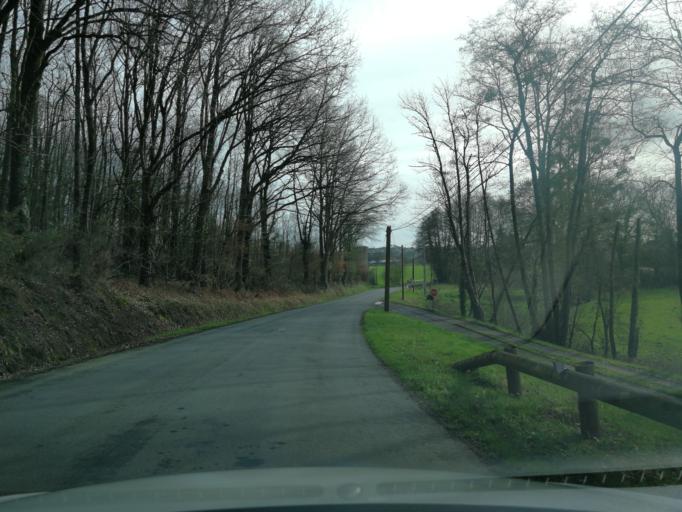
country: FR
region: Brittany
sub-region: Departement d'Ille-et-Vilaine
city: Pance
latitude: 47.8958
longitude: -1.6995
